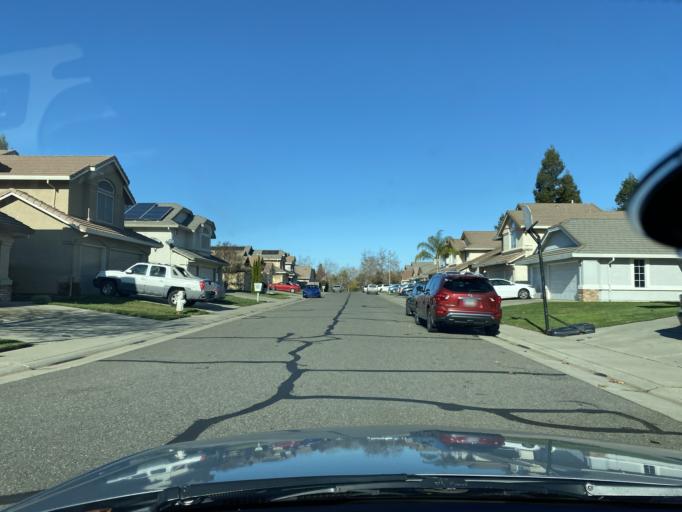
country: US
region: California
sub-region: Sacramento County
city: Elk Grove
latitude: 38.4326
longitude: -121.3815
